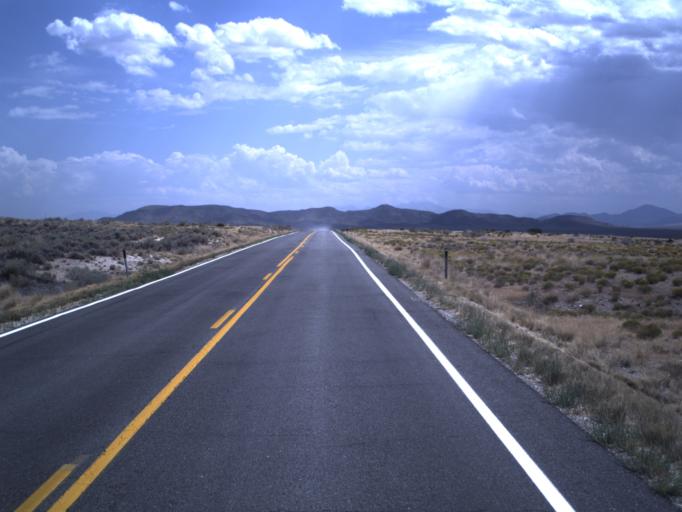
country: US
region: Utah
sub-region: Utah County
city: Eagle Mountain
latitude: 40.2615
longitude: -112.2324
